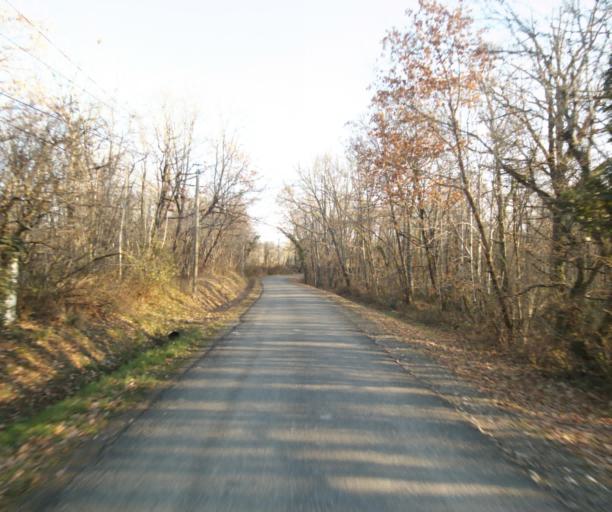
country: FR
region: Midi-Pyrenees
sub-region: Departement du Tarn-et-Garonne
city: Moissac
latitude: 44.1537
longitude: 1.1406
